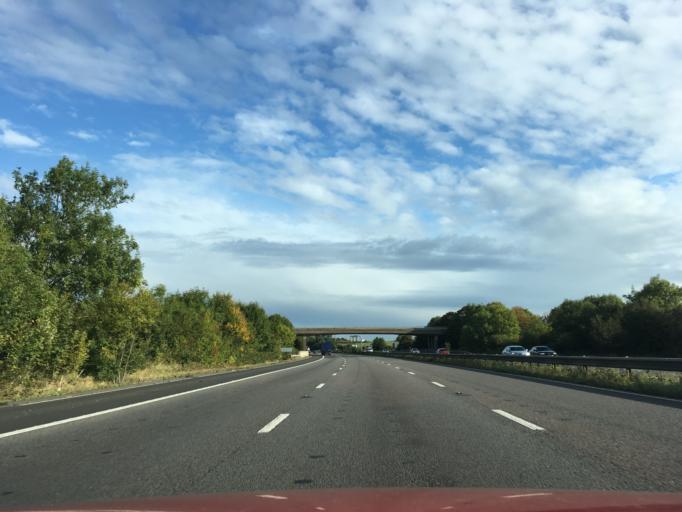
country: GB
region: England
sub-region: Gloucestershire
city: Churchdown
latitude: 51.8775
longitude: -2.1517
